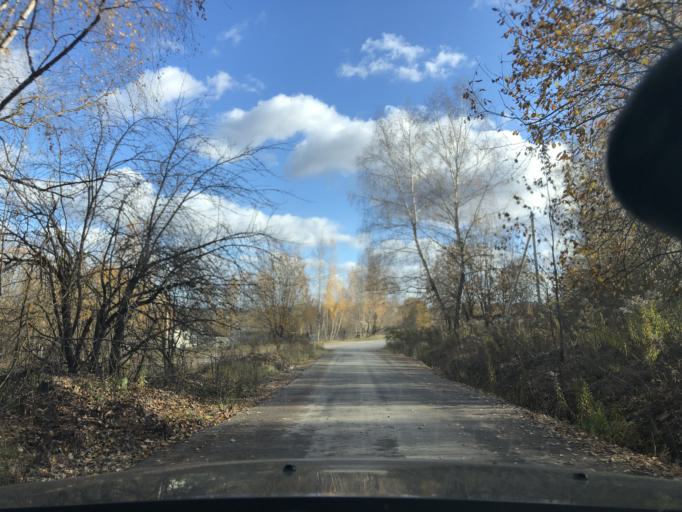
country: RU
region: Tula
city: Gorelki
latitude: 54.2952
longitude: 37.5537
